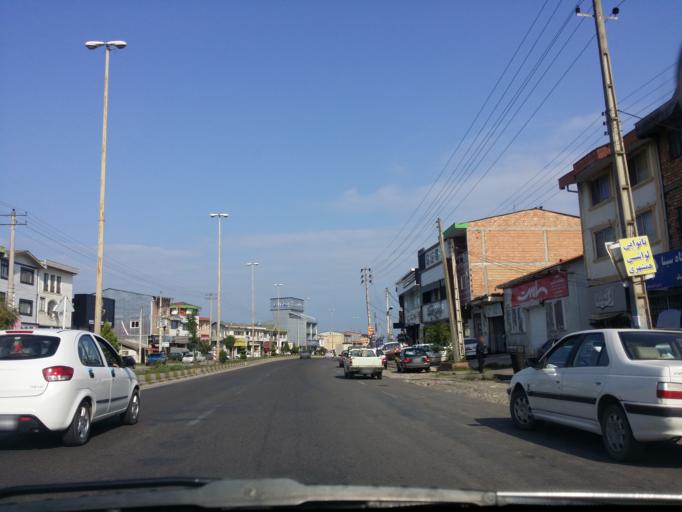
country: IR
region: Mazandaran
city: Chalus
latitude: 36.6781
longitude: 51.4034
